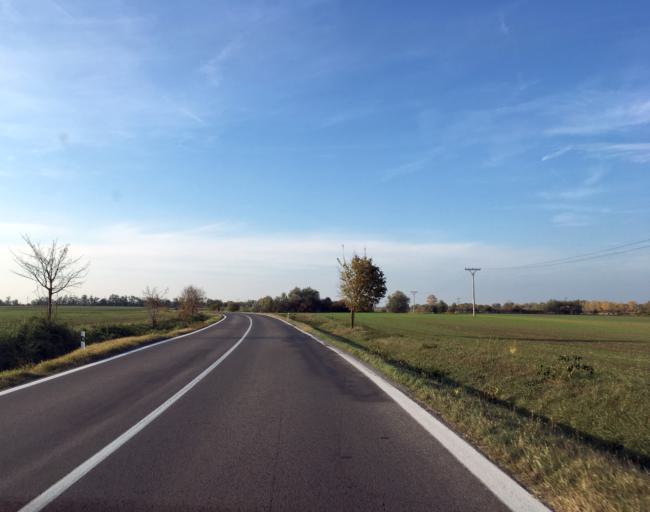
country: SK
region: Nitriansky
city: Surany
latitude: 48.0519
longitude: 18.1118
